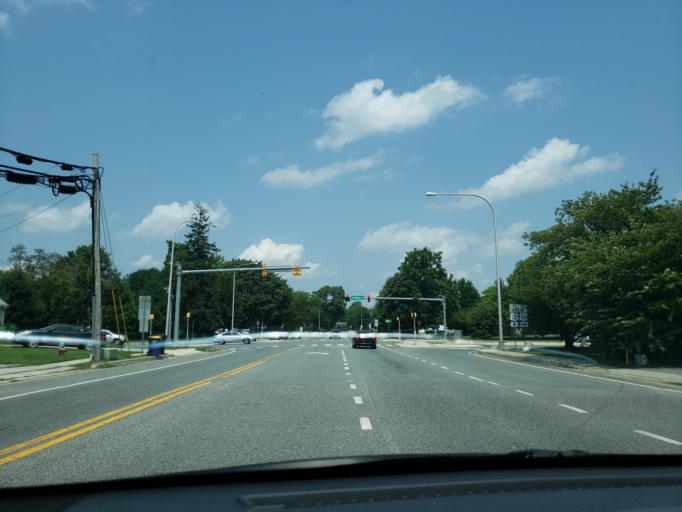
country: US
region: Delaware
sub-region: Kent County
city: Rodney Village
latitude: 39.1326
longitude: -75.5301
